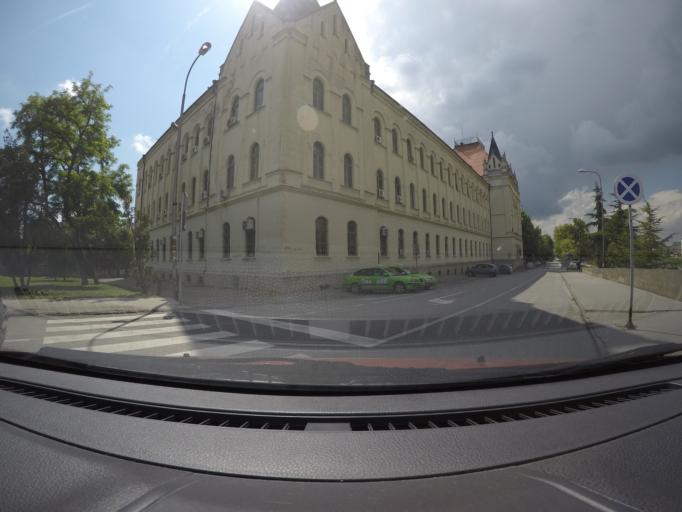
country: RS
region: Autonomna Pokrajina Vojvodina
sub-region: Srednjebanatski Okrug
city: Zrenjanin
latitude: 45.3789
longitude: 20.3892
